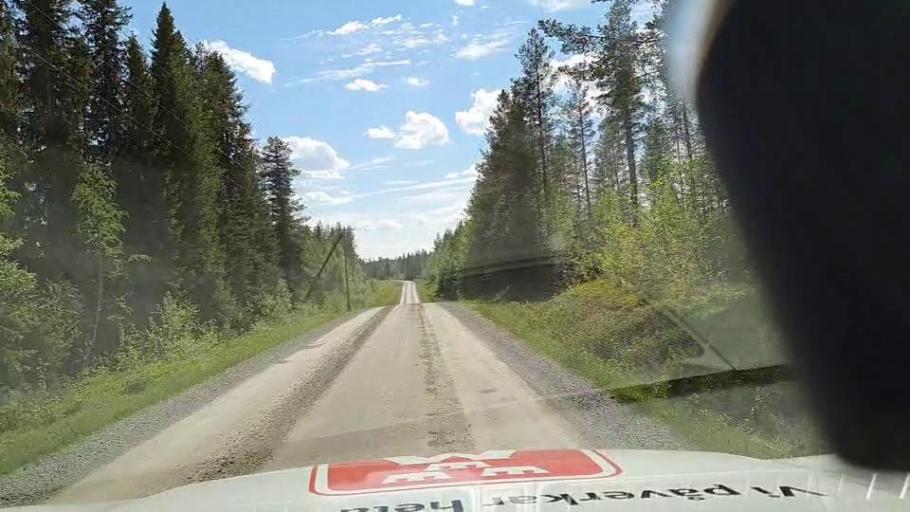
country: SE
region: Jaemtland
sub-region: Stroemsunds Kommun
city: Stroemsund
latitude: 64.4643
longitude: 15.5939
